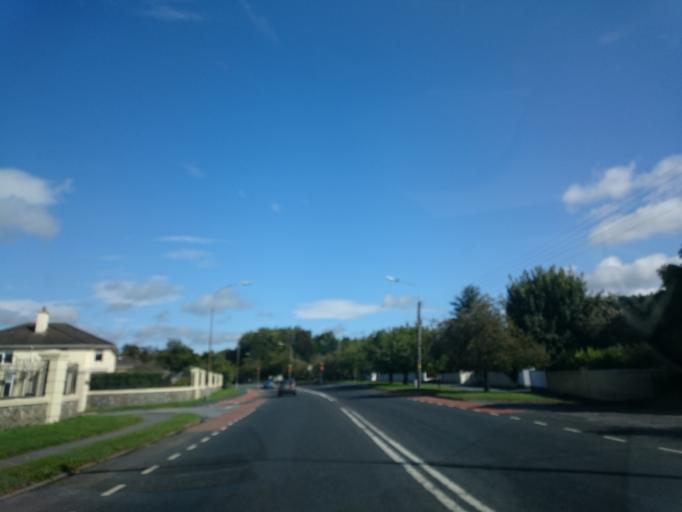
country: IE
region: Leinster
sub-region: Kilkenny
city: Kilkenny
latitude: 52.6689
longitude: -7.2526
